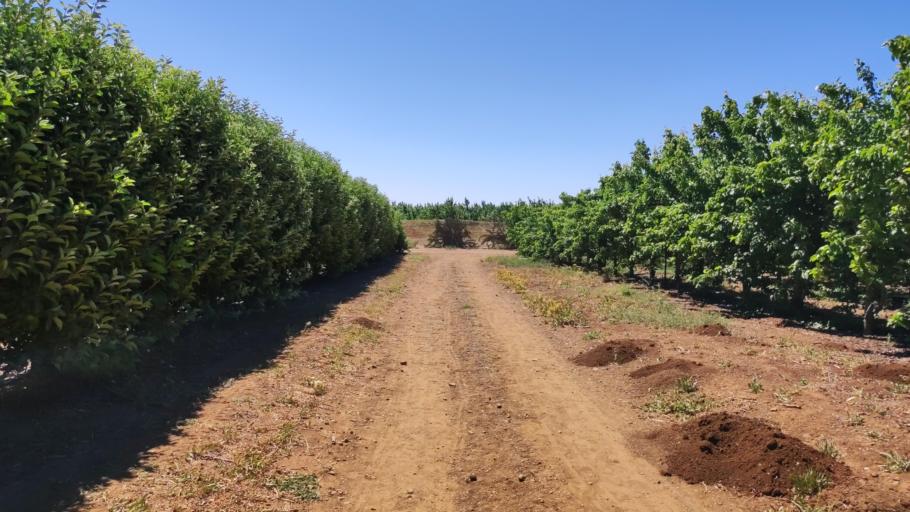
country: SY
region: Quneitra
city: Al Qunaytirah
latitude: 33.1202
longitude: 35.8066
